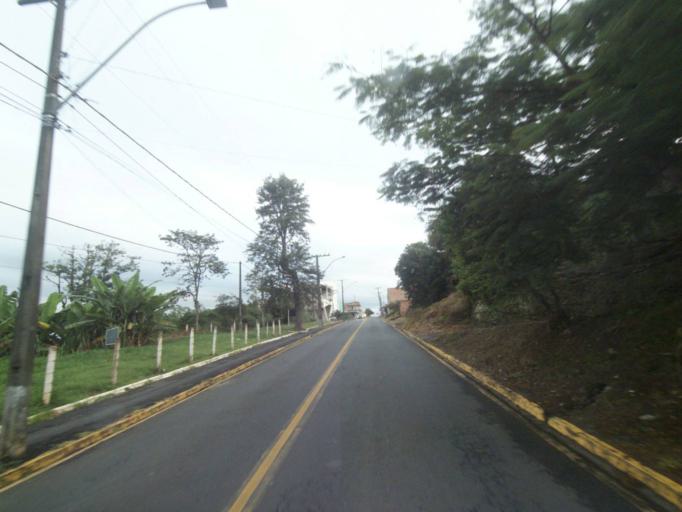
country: BR
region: Parana
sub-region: Telemaco Borba
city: Telemaco Borba
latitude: -24.3177
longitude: -50.6170
